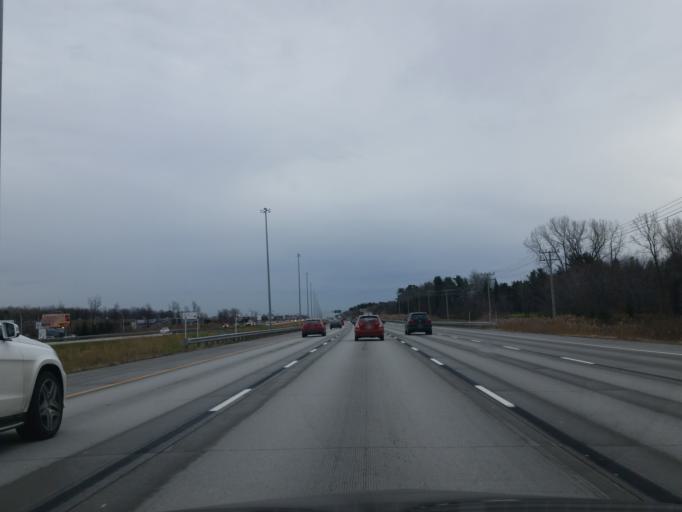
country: CA
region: Quebec
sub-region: Laurentides
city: Blainville
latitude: 45.6732
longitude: -73.9090
